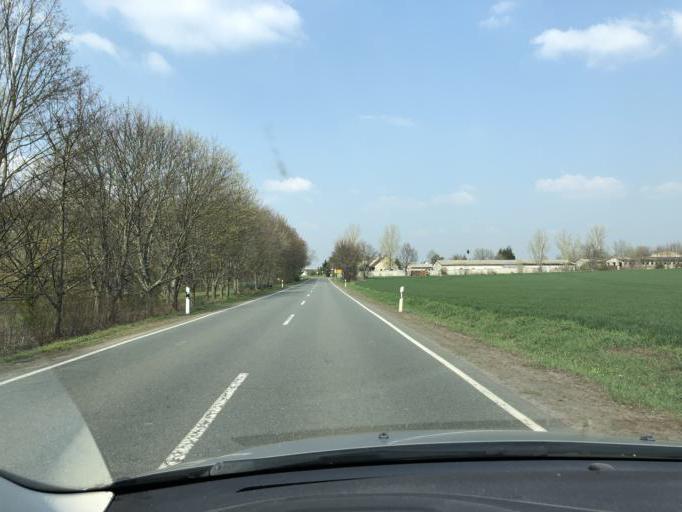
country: DE
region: Saxony-Anhalt
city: Zorbig
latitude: 51.5816
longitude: 12.1415
